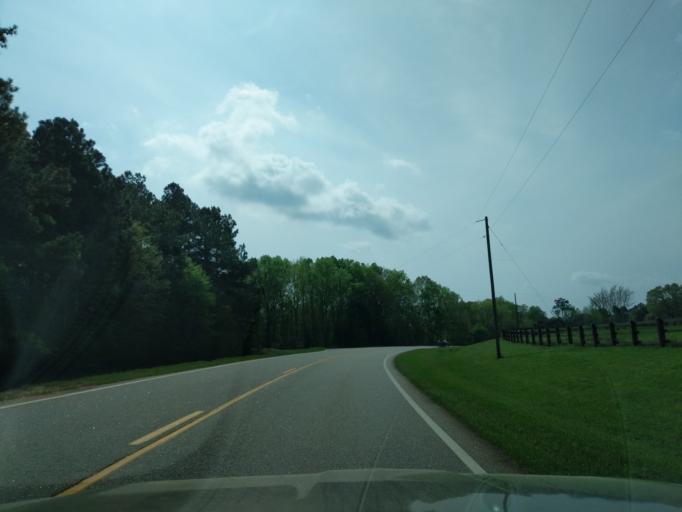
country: US
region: Georgia
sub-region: Lincoln County
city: Lincolnton
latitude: 33.7911
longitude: -82.3808
